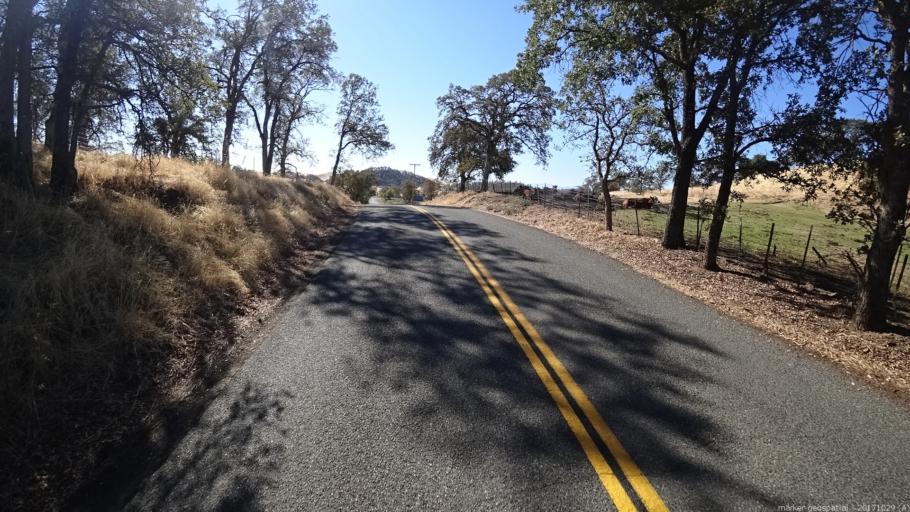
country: US
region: California
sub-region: Shasta County
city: Shasta
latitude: 40.4538
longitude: -122.6348
